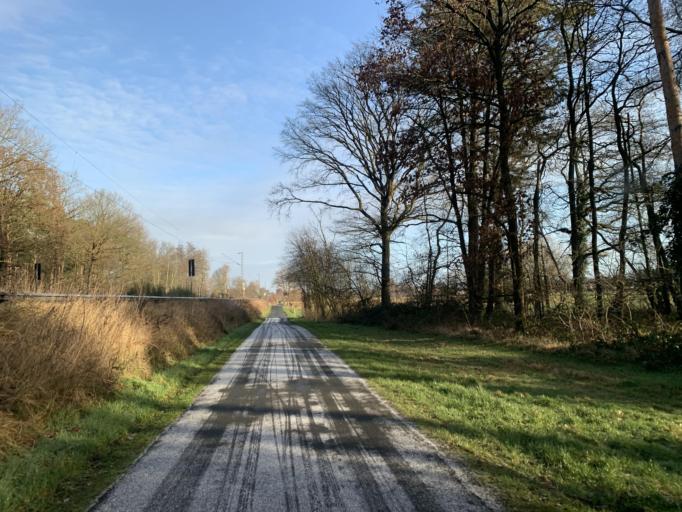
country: DE
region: North Rhine-Westphalia
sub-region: Regierungsbezirk Munster
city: Dulmen
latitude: 51.7989
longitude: 7.2589
